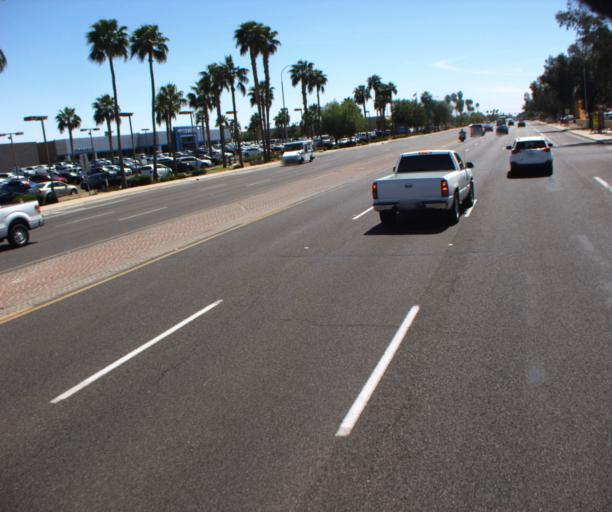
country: US
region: Arizona
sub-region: Maricopa County
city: San Carlos
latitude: 33.3399
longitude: -111.8419
